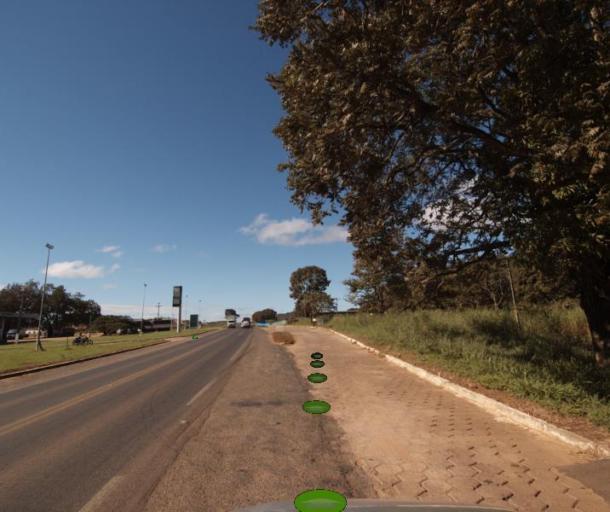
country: BR
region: Goias
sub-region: Uruacu
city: Uruacu
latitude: -14.5414
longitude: -49.1622
